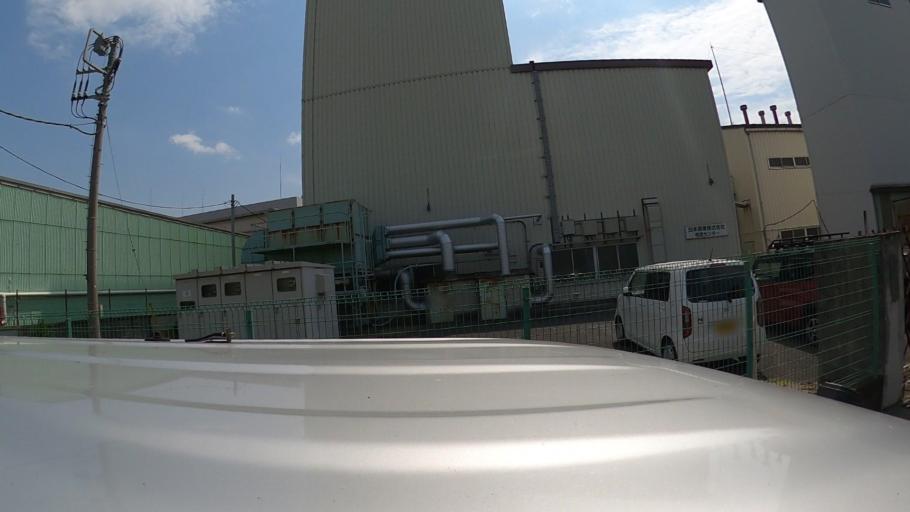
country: JP
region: Kanagawa
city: Chigasaki
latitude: 35.3542
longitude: 139.3733
